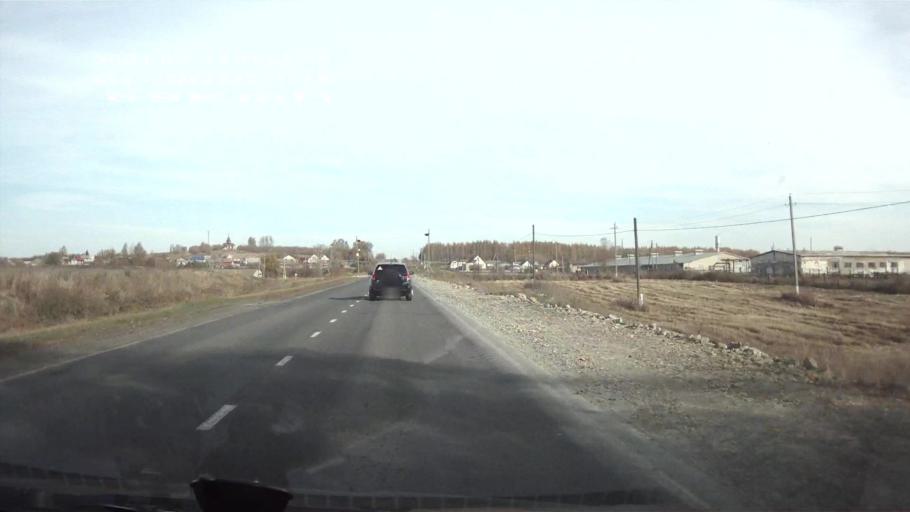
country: RU
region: Mordoviya
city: Atyashevo
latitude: 54.5599
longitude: 45.9752
